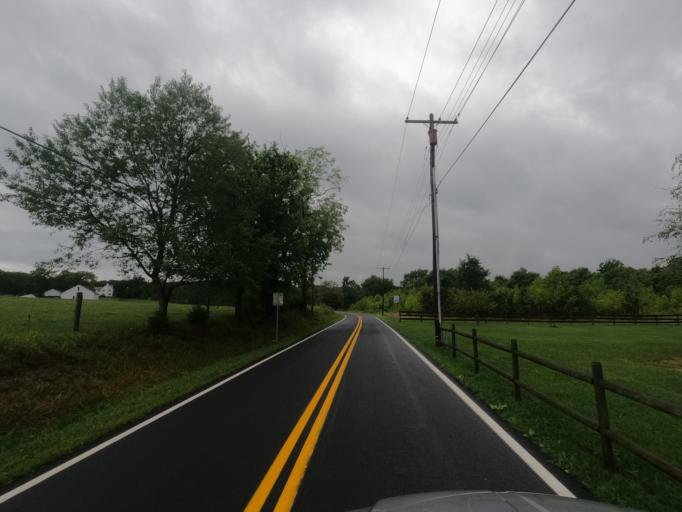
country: US
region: West Virginia
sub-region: Berkeley County
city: Martinsburg
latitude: 39.6201
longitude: -78.0118
